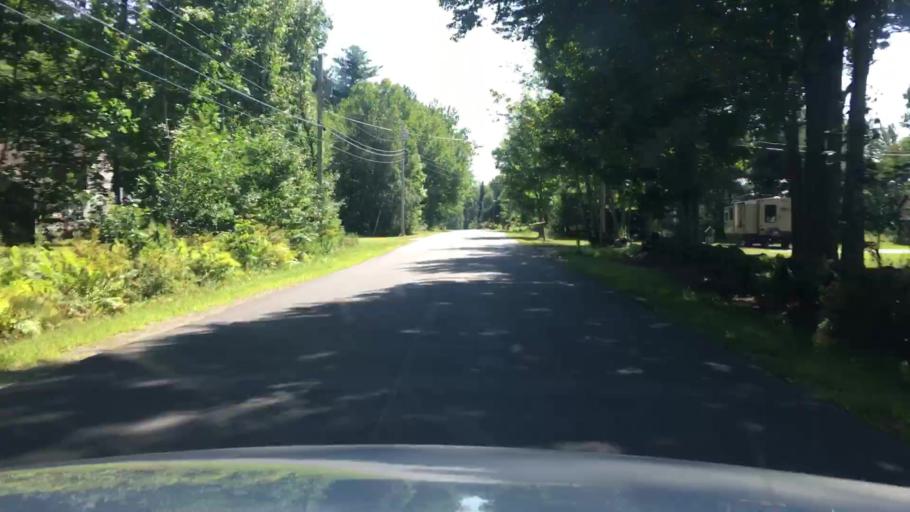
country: US
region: Maine
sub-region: Kennebec County
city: Monmouth
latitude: 44.2601
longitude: -70.0554
